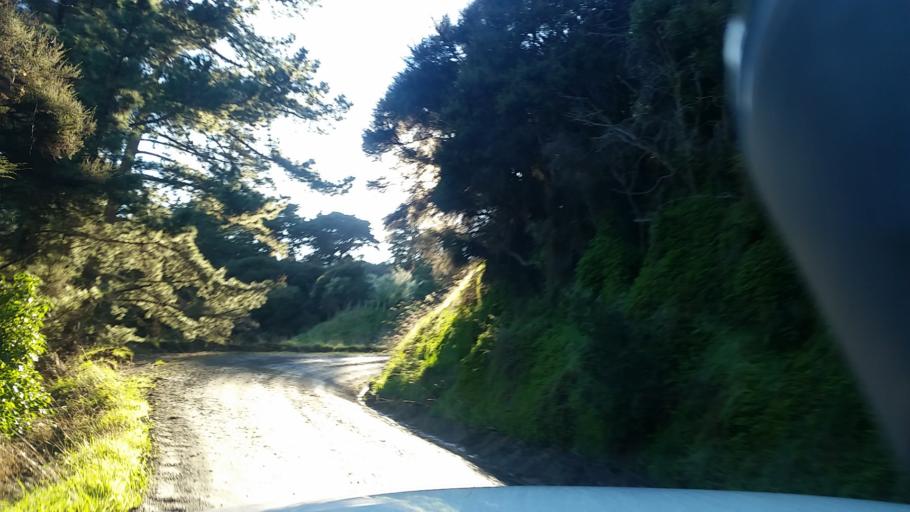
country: NZ
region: Canterbury
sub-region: Christchurch City
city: Christchurch
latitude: -43.7021
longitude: 173.0593
